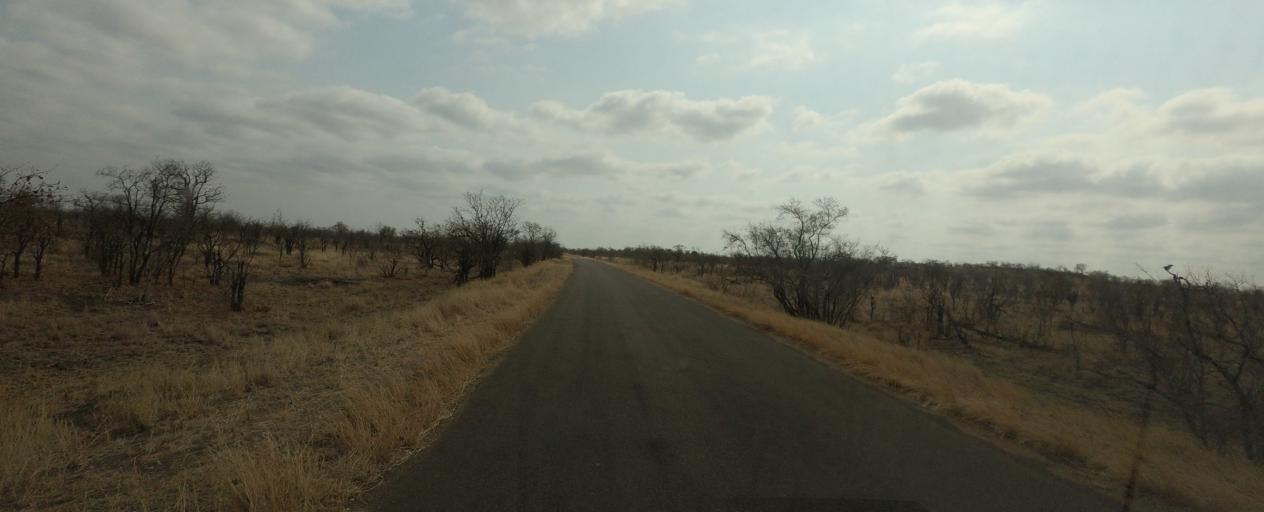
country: ZA
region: Limpopo
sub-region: Vhembe District Municipality
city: Mutale
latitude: -22.5733
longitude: 31.1894
